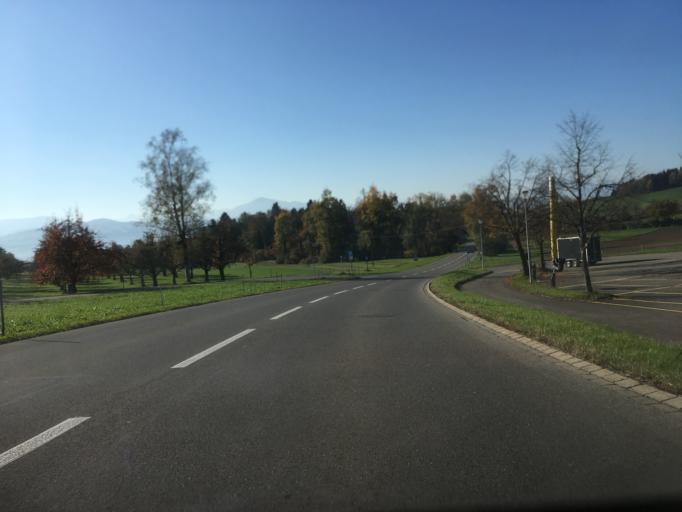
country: CH
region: Zurich
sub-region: Bezirk Affoltern
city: Hausen am Albis / Hausen (Dorf)
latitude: 47.2265
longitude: 8.5267
